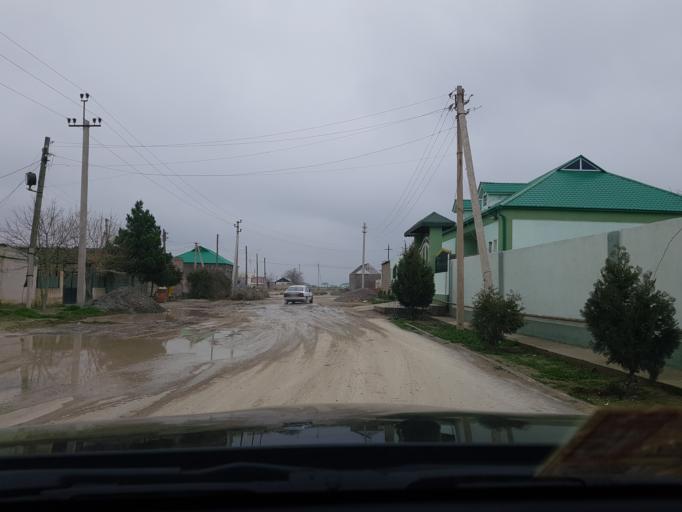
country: TM
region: Ahal
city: Abadan
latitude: 38.1416
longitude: 57.9477
